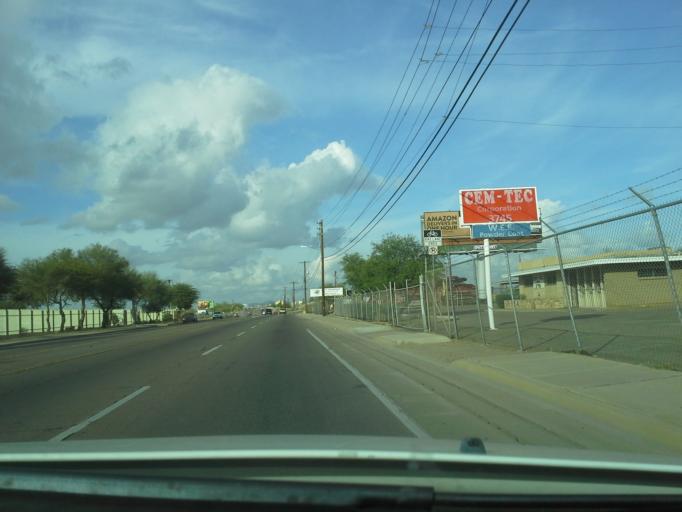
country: US
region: Arizona
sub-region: Maricopa County
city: Phoenix
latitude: 33.4125
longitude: -112.0820
